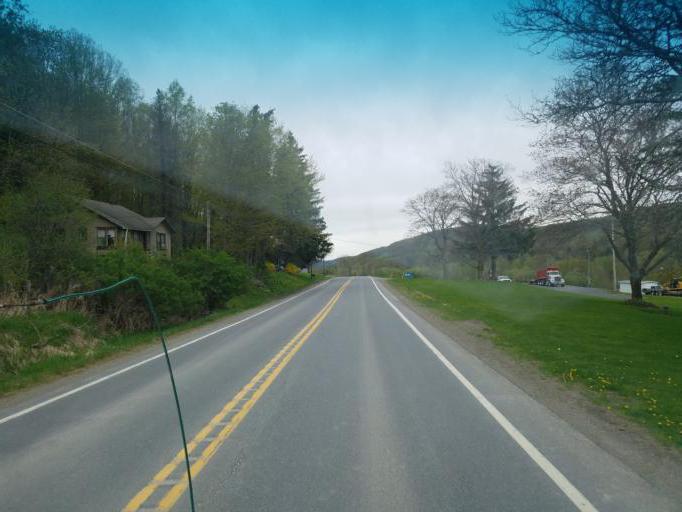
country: US
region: Pennsylvania
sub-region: Tioga County
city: Westfield
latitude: 41.8752
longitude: -77.5229
